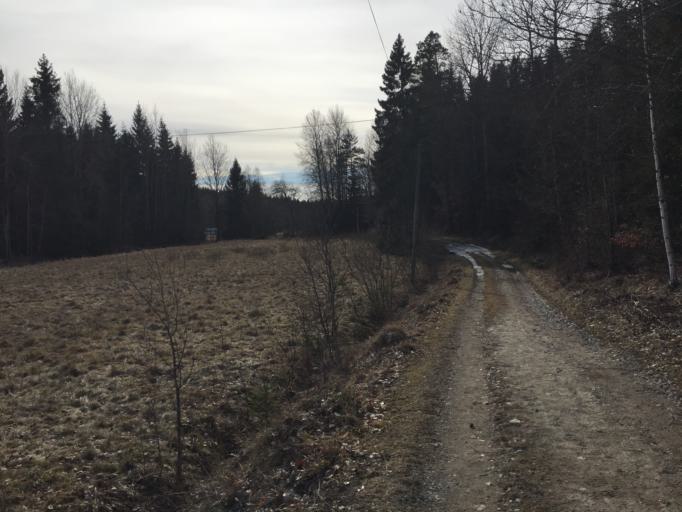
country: SE
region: Stockholm
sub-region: Botkyrka Kommun
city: Tullinge
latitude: 59.0966
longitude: 17.9668
